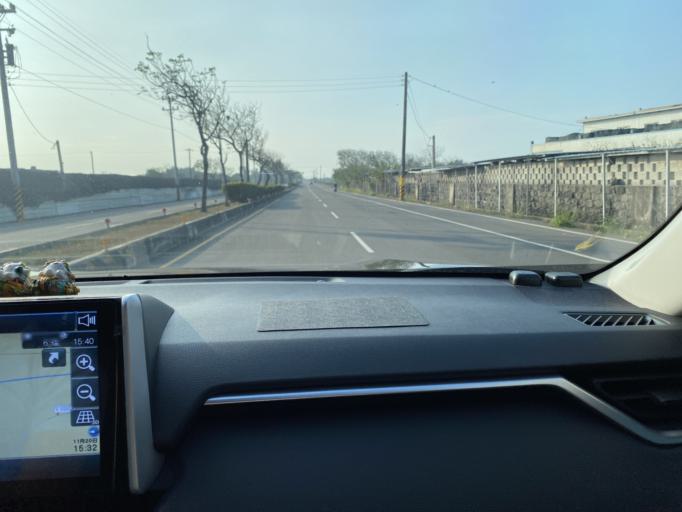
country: TW
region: Taiwan
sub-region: Changhua
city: Chang-hua
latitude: 23.9591
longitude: 120.3998
